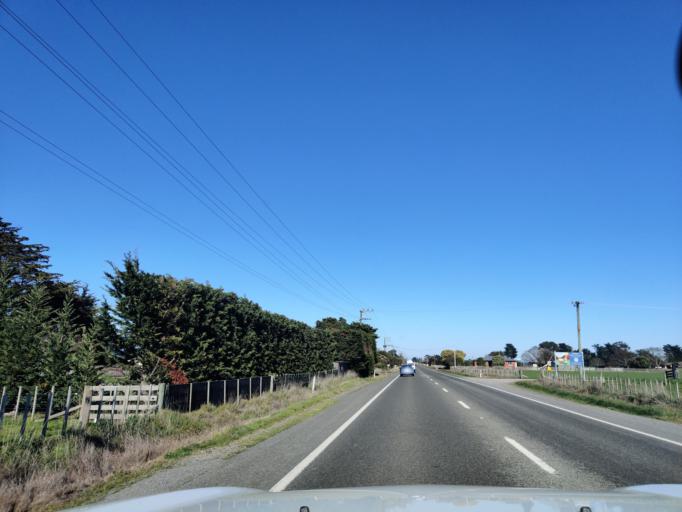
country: NZ
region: Manawatu-Wanganui
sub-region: Palmerston North City
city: Palmerston North
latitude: -40.2565
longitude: 175.5752
